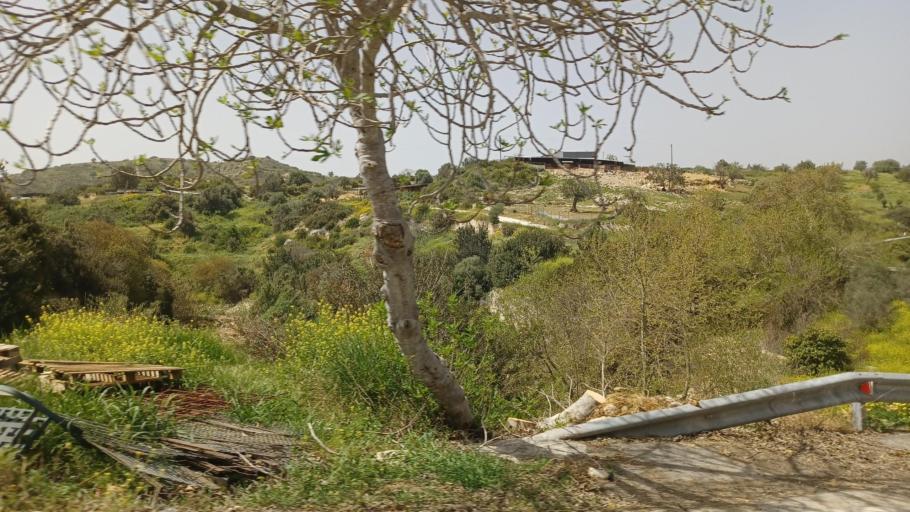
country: CY
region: Limassol
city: Pissouri
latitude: 34.6967
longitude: 32.7597
